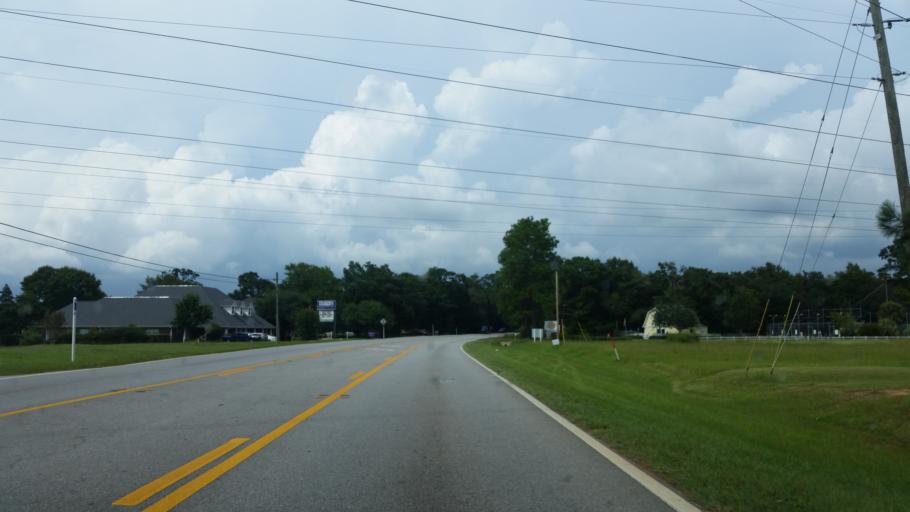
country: US
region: Florida
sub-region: Santa Rosa County
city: Wallace
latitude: 30.6378
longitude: -87.1818
